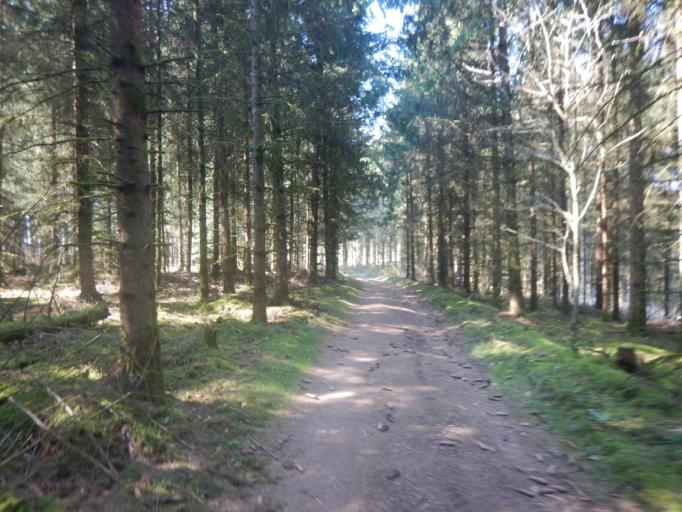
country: LU
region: Diekirch
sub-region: Canton de Clervaux
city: Clervaux
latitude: 50.0532
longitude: 5.9916
